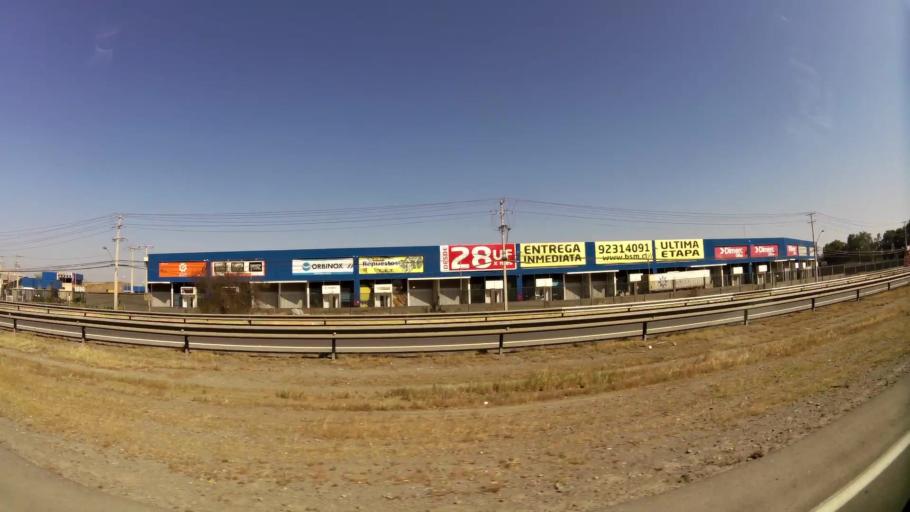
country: CL
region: Santiago Metropolitan
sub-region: Provincia de Chacabuco
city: Chicureo Abajo
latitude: -33.3477
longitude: -70.6939
